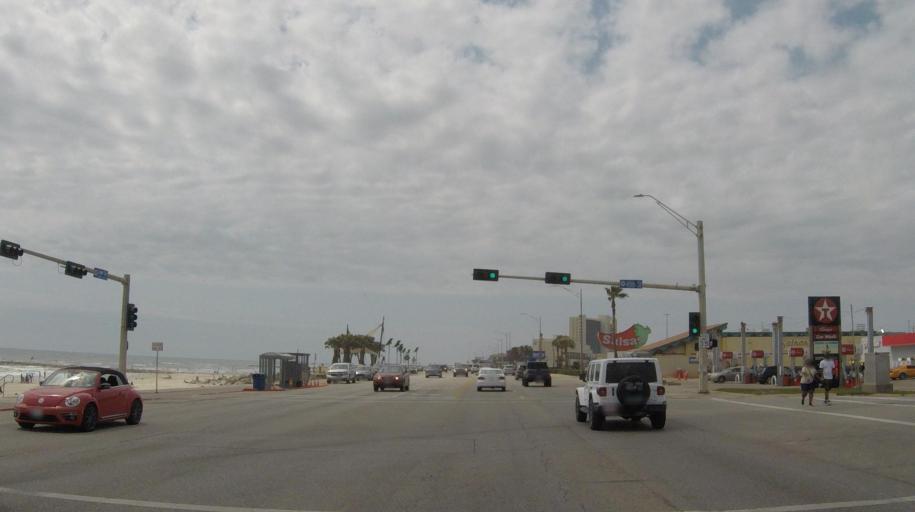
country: US
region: Texas
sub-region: Galveston County
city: Galveston
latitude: 29.2757
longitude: -94.8105
